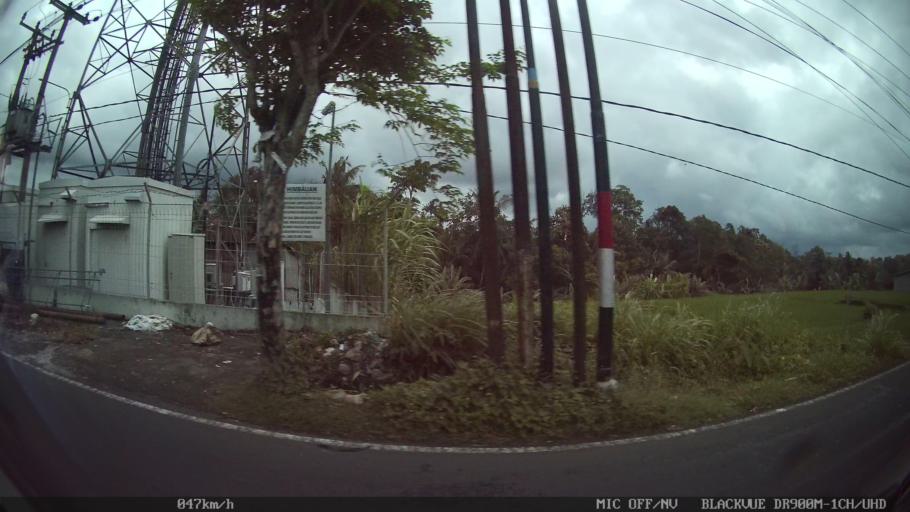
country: ID
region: Bali
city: Banjar Pekenjelodan
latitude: -8.5635
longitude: 115.1775
